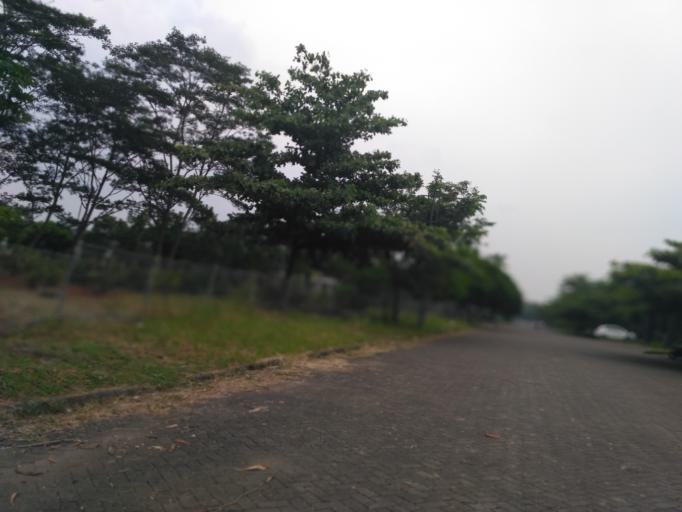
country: ID
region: Central Java
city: Semarang
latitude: -7.0633
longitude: 110.4341
